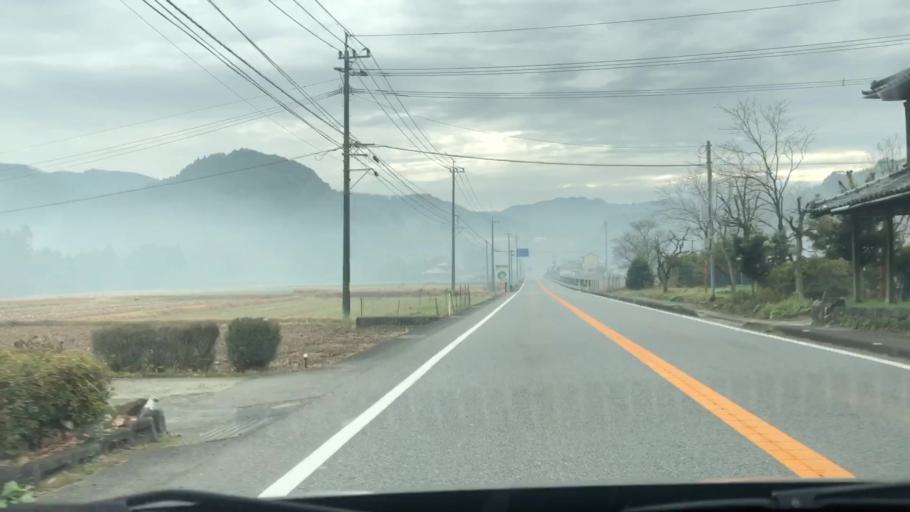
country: JP
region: Oita
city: Usuki
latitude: 33.0205
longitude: 131.6976
